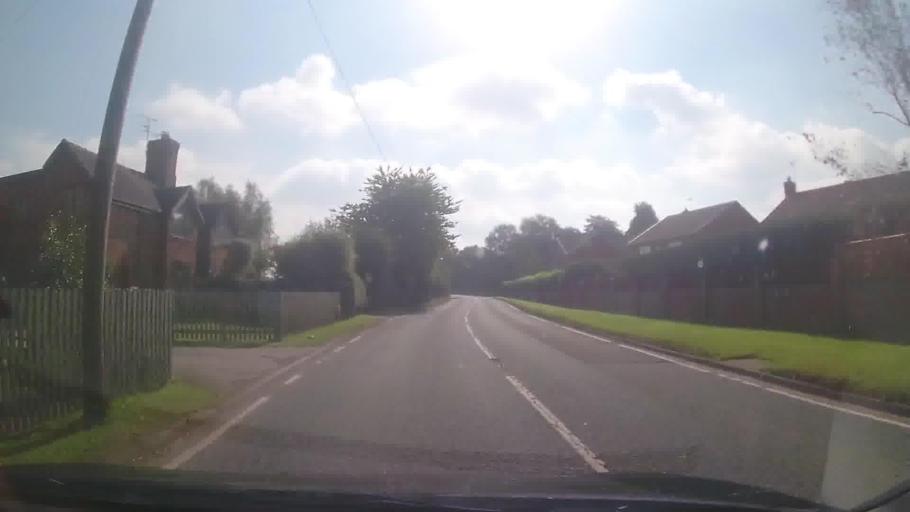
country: GB
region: England
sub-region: Cheshire West and Chester
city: Beeston
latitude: 53.1062
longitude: -2.6615
